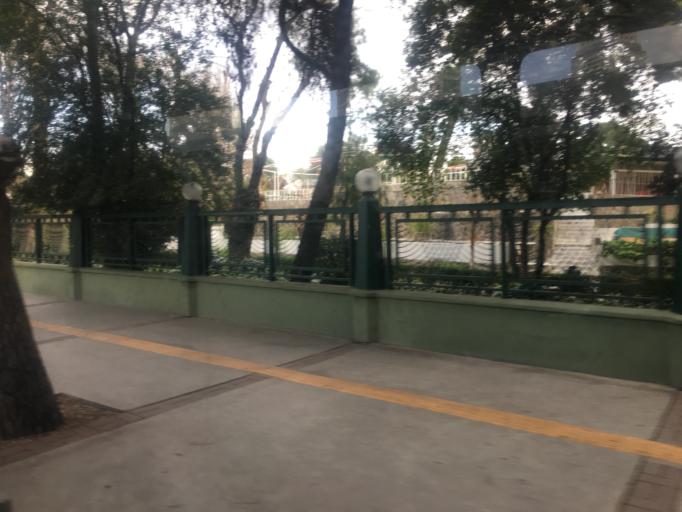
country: TR
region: Izmir
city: Izmir
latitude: 38.4258
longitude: 27.1421
